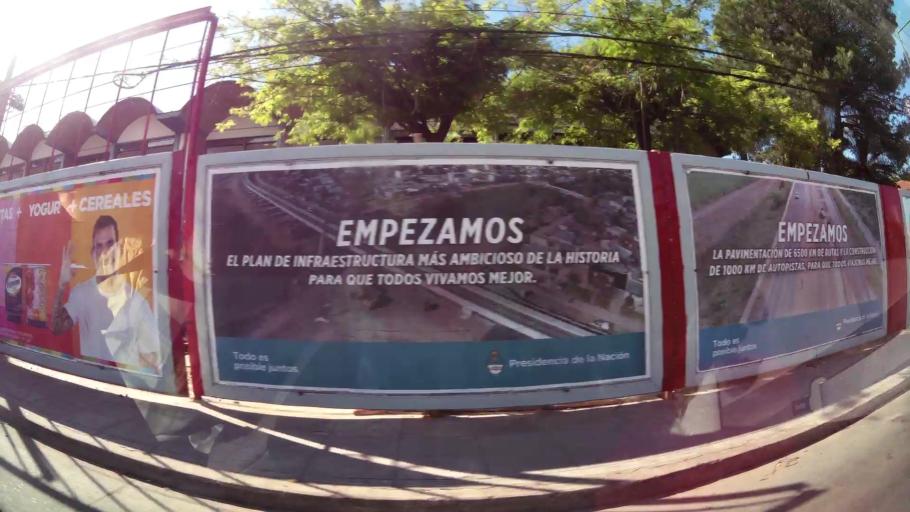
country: AR
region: Buenos Aires
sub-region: Partido de Tigre
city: Tigre
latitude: -34.4743
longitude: -58.5725
